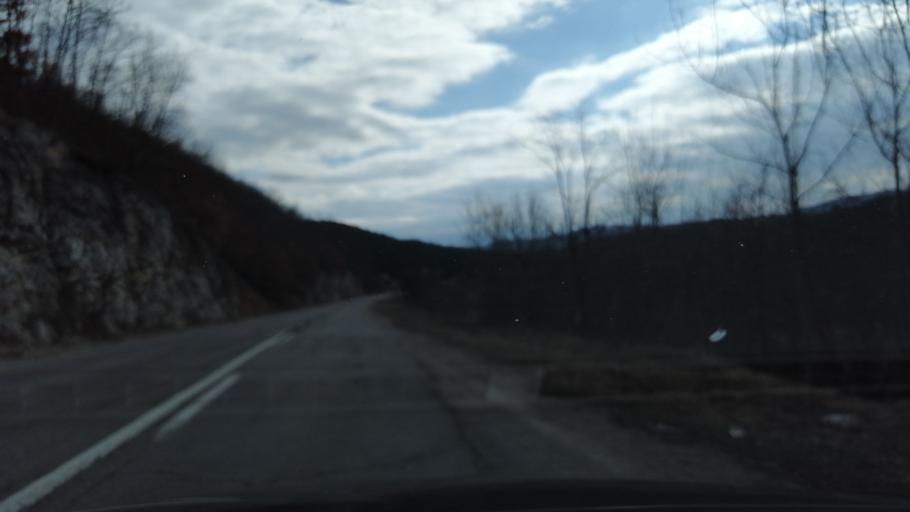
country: RS
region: Central Serbia
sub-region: Zlatiborski Okrug
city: Cajetina
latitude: 43.7975
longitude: 19.6533
